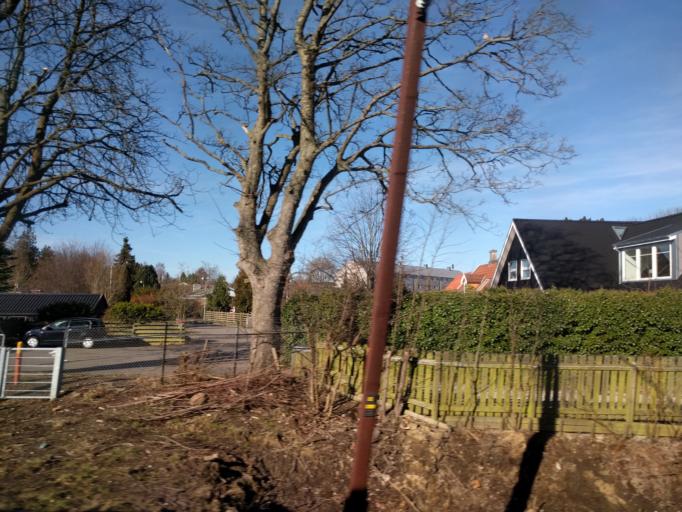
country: DK
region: Capital Region
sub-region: Fredensborg Kommune
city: Humlebaek
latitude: 55.9809
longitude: 12.5455
